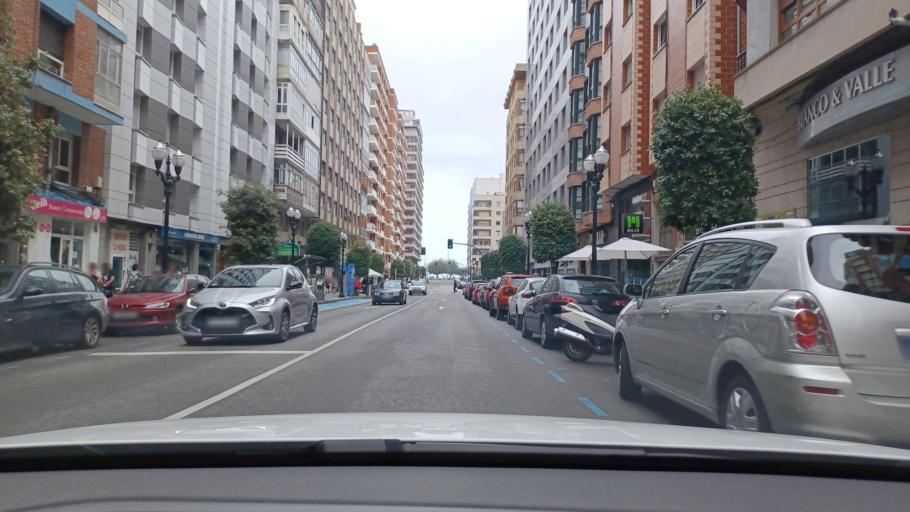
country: ES
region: Asturias
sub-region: Province of Asturias
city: Gijon
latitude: 43.5383
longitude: -5.6525
